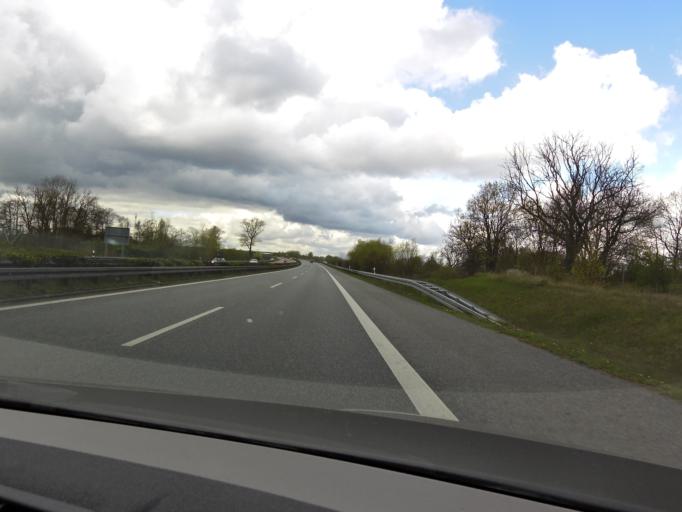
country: DE
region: Mecklenburg-Vorpommern
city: Broderstorf
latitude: 54.0401
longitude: 12.3370
